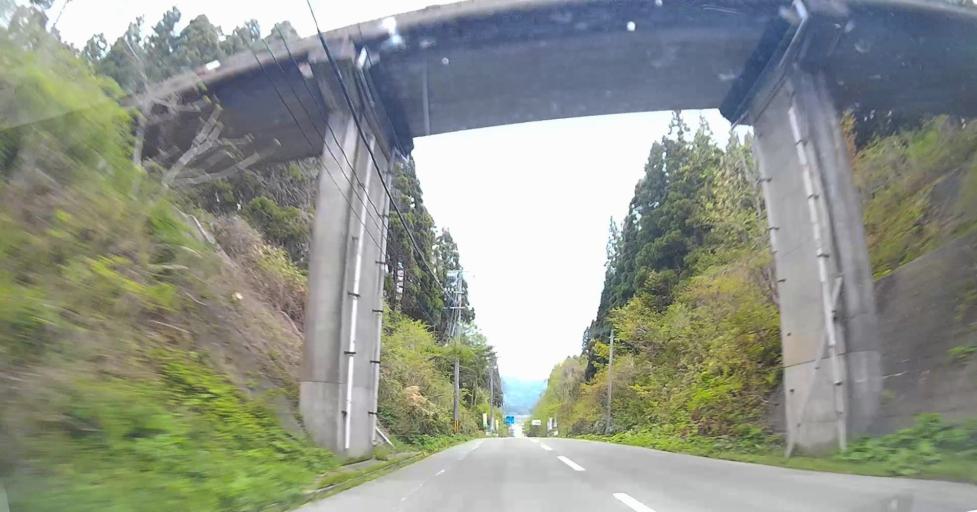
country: JP
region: Aomori
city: Goshogawara
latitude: 41.1770
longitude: 140.4857
